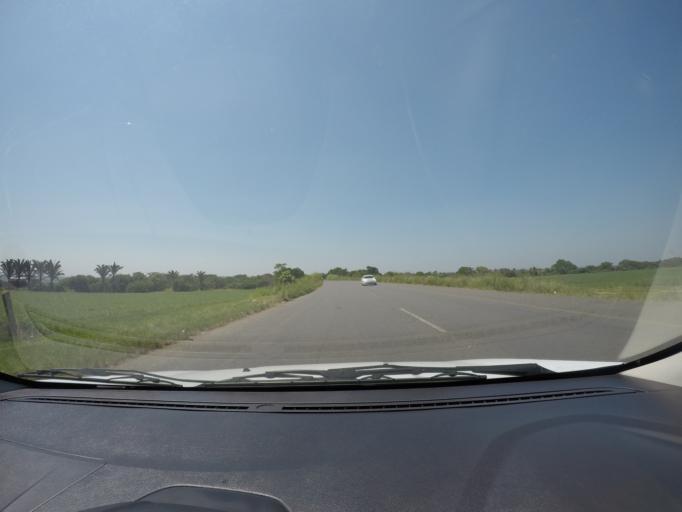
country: ZA
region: KwaZulu-Natal
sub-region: uThungulu District Municipality
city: Empangeni
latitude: -28.8025
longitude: 31.9584
